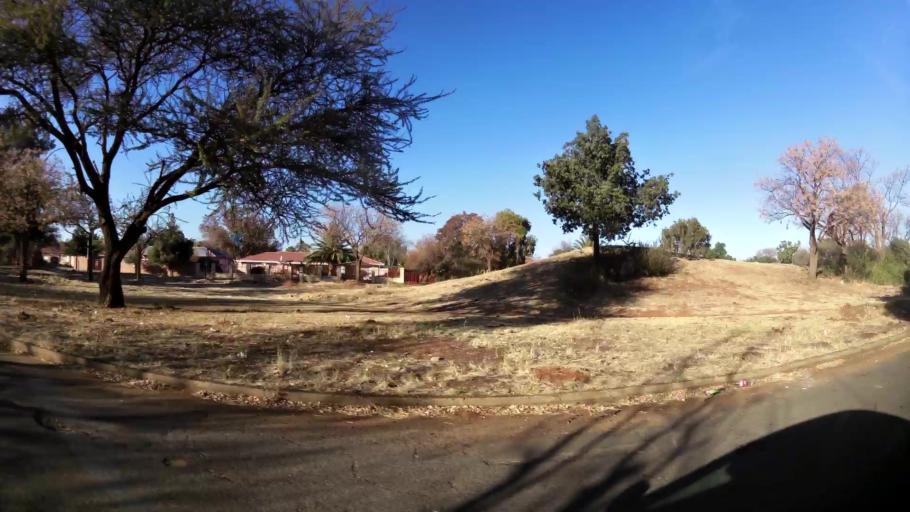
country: ZA
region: Northern Cape
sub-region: Frances Baard District Municipality
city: Kimberley
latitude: -28.7388
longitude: 24.7351
